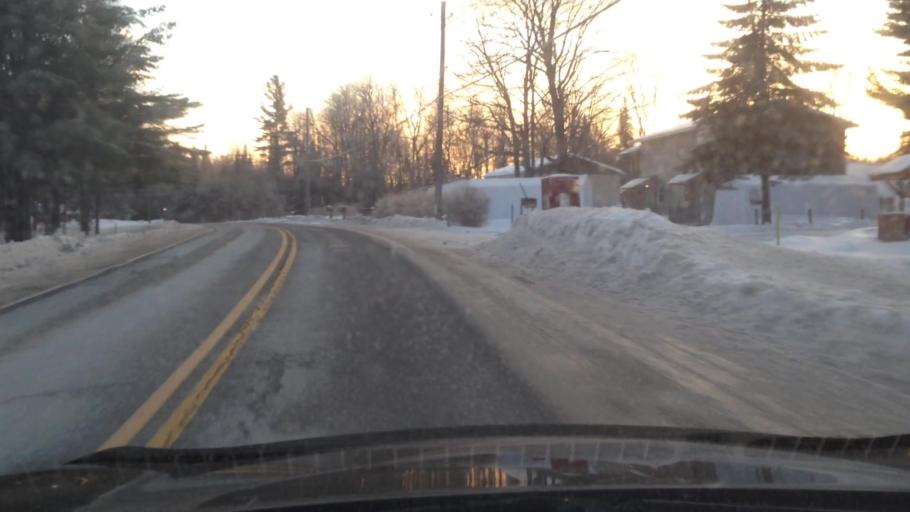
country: CA
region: Quebec
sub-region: Lanaudiere
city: Sainte-Julienne
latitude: 45.9324
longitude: -73.7407
